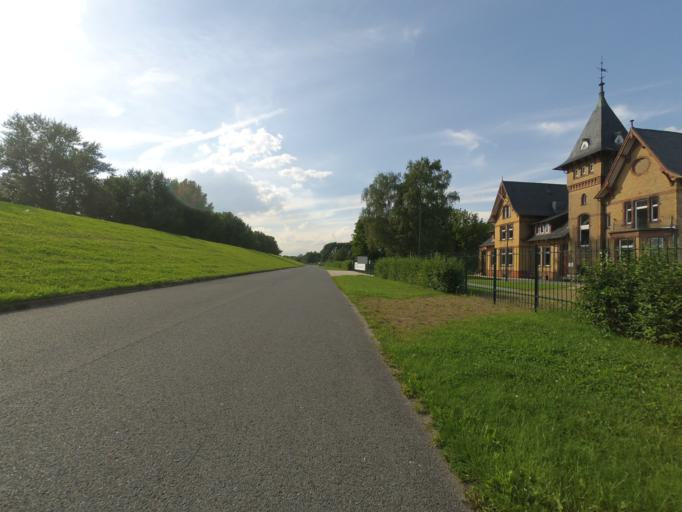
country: DE
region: Hamburg
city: Rothenburgsort
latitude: 53.5239
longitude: 10.0526
